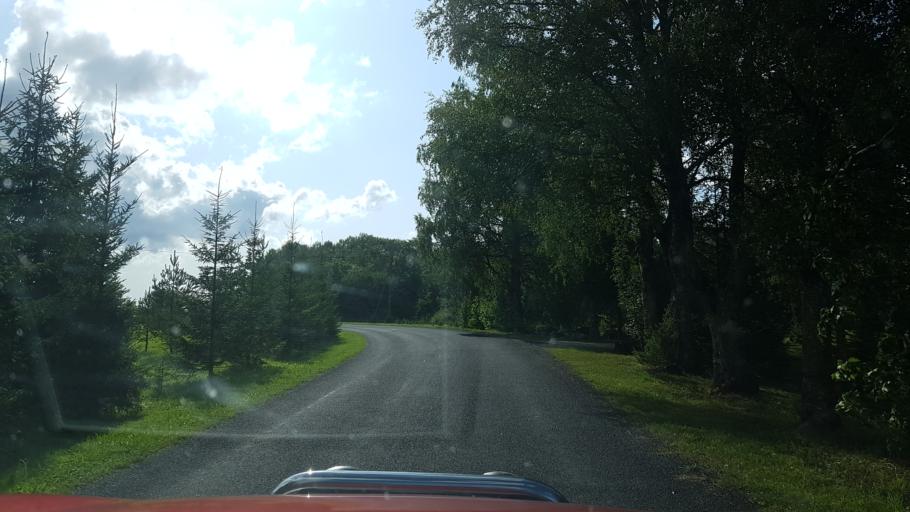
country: EE
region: Harju
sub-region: Paldiski linn
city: Paldiski
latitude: 59.2004
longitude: 23.9661
